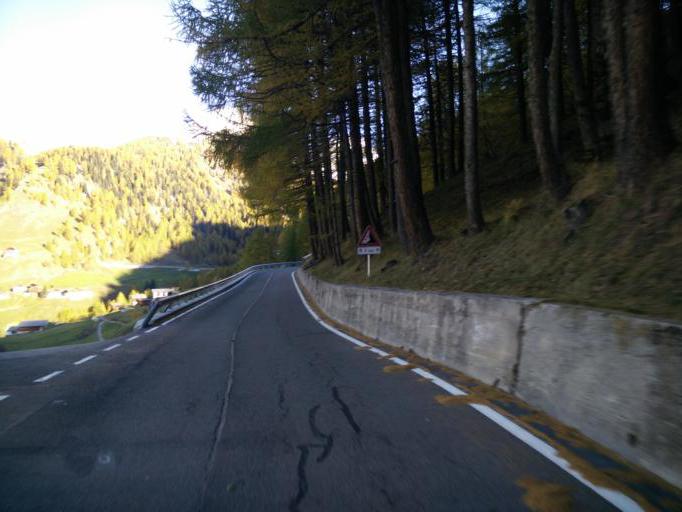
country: IT
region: Trentino-Alto Adige
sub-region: Bolzano
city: Moso in Passiria
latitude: 46.8696
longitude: 11.1604
